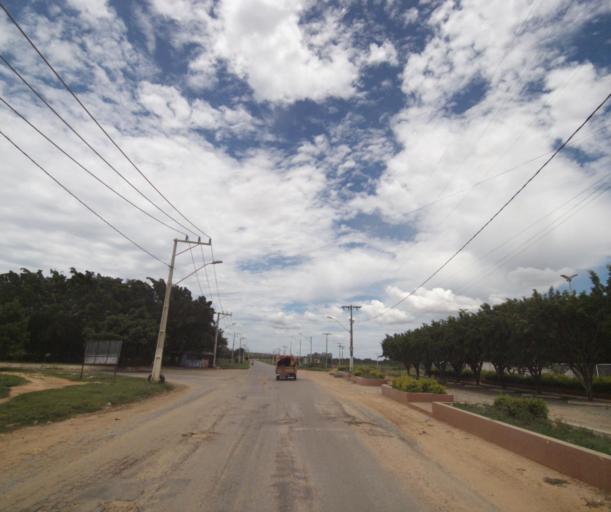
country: BR
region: Bahia
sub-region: Carinhanha
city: Carinhanha
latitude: -14.3334
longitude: -43.7706
